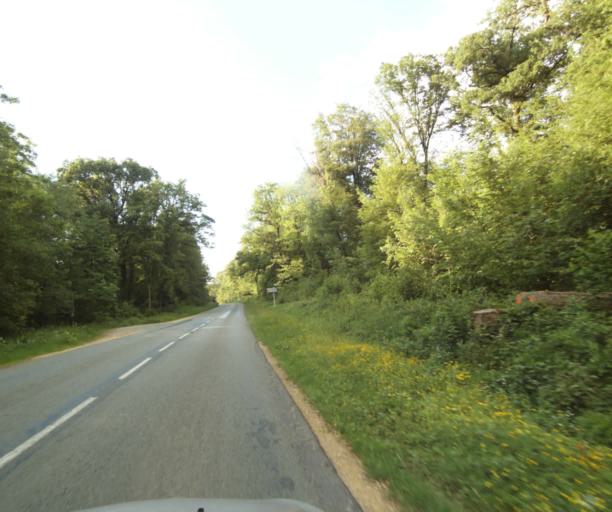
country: FR
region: Champagne-Ardenne
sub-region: Departement des Ardennes
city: Warcq
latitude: 49.8180
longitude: 4.6998
